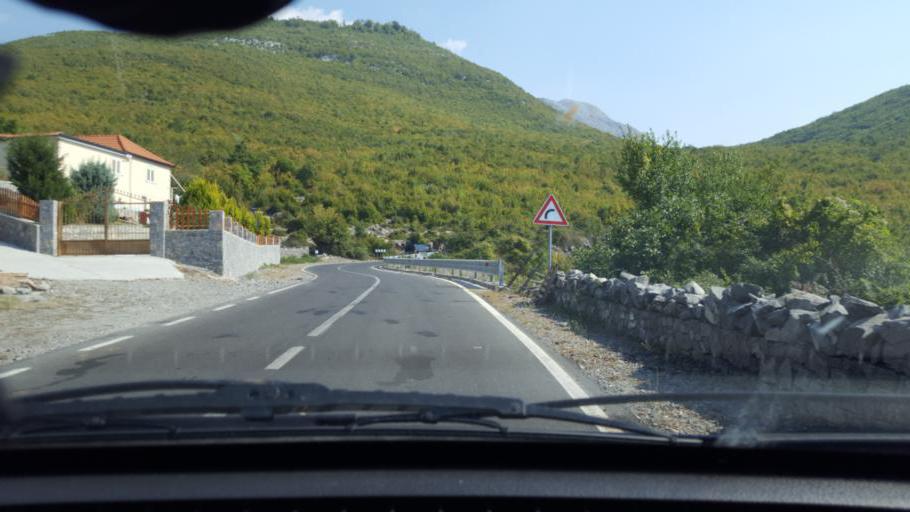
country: AL
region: Shkoder
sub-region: Rrethi i Malesia e Madhe
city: Kastrat
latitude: 42.3838
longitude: 19.4935
